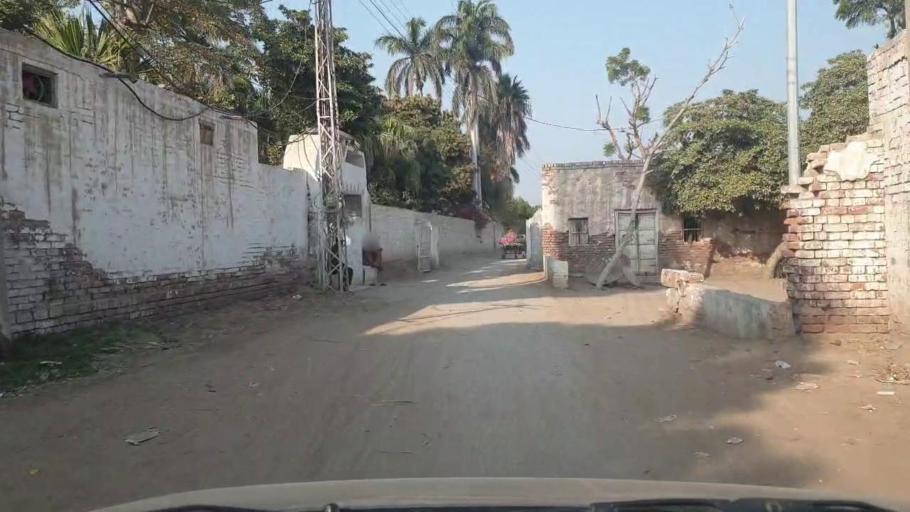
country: PK
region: Sindh
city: Digri
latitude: 25.2534
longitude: 69.1790
